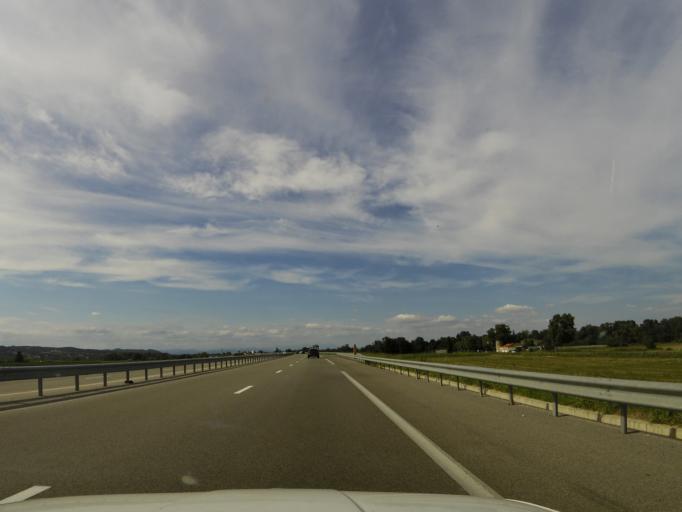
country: FR
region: Languedoc-Roussillon
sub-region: Departement du Gard
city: La Calmette
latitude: 43.9473
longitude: 4.2488
